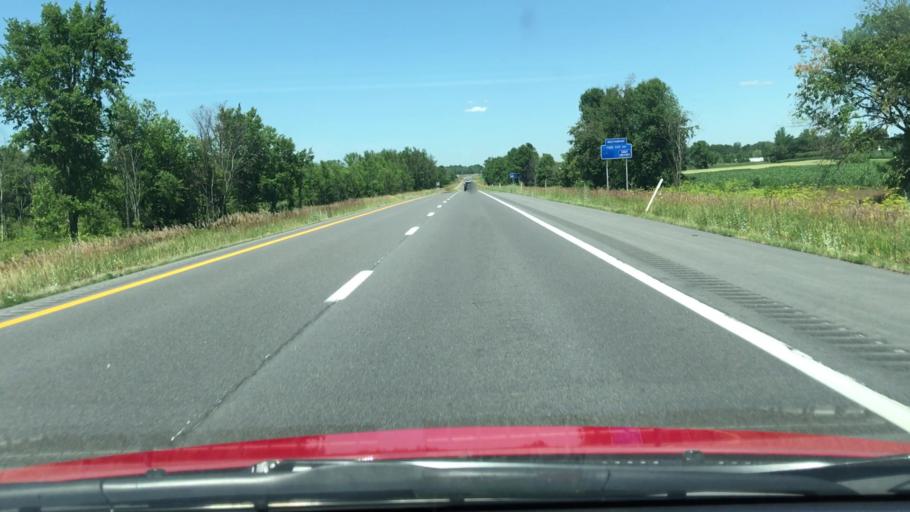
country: US
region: New York
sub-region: Clinton County
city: Cumberland Head
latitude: 44.7709
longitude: -73.4337
